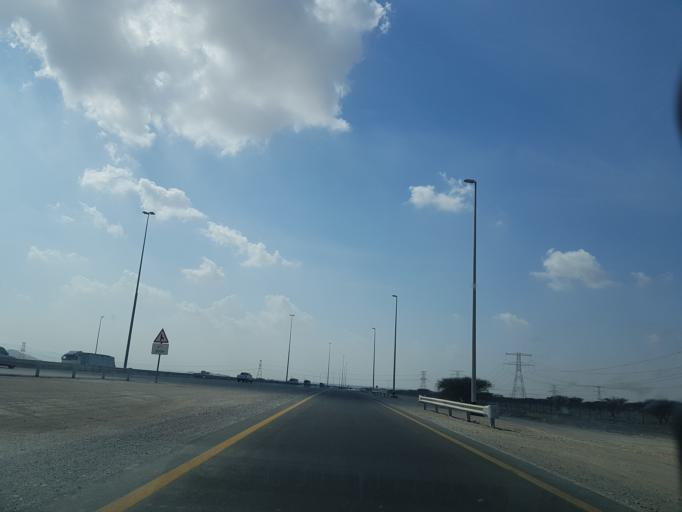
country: AE
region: Ra's al Khaymah
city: Ras al-Khaimah
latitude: 25.7604
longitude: 56.0206
